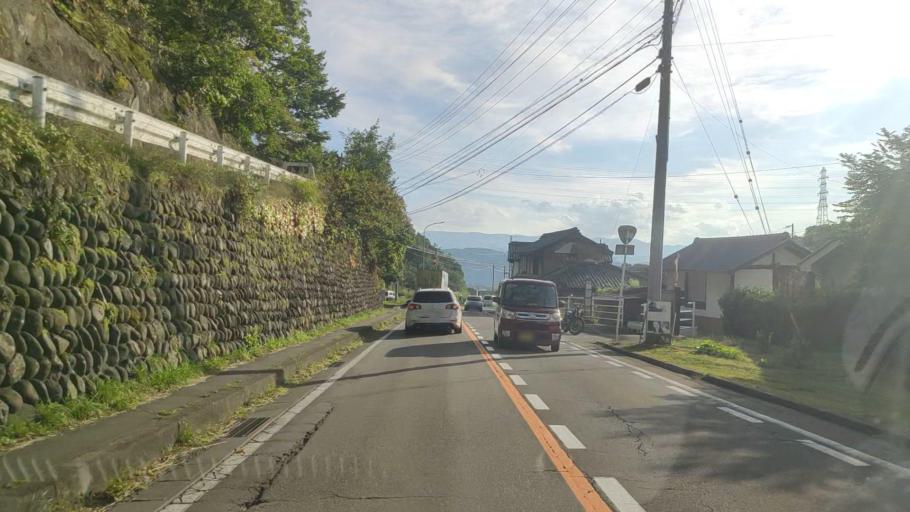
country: JP
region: Nagano
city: Ueda
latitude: 36.4173
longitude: 138.2953
